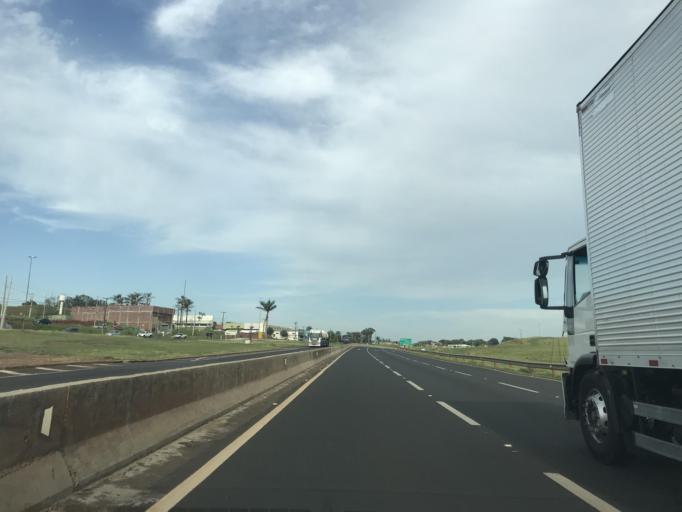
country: BR
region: Parana
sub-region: Mandaguacu
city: Mandaguacu
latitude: -23.3379
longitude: -52.1024
